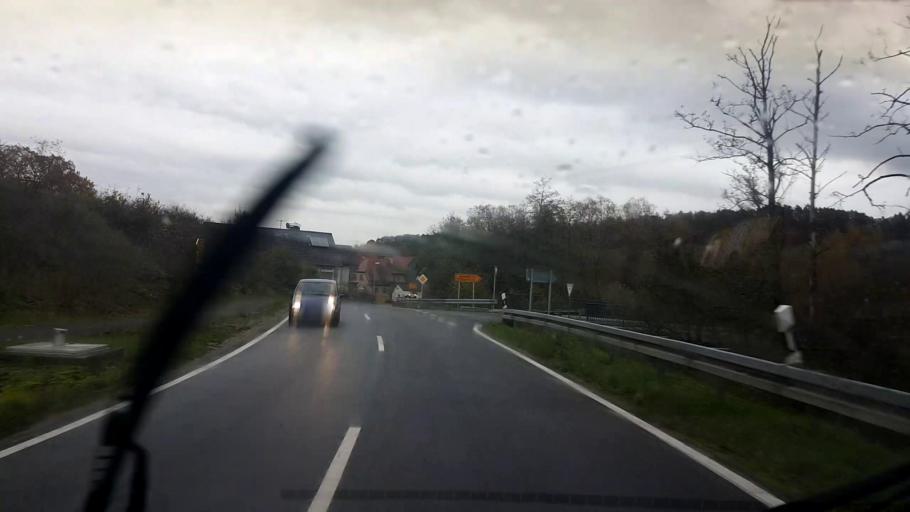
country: DE
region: Bavaria
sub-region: Upper Franconia
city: Burgwindheim
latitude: 49.8799
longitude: 10.5964
